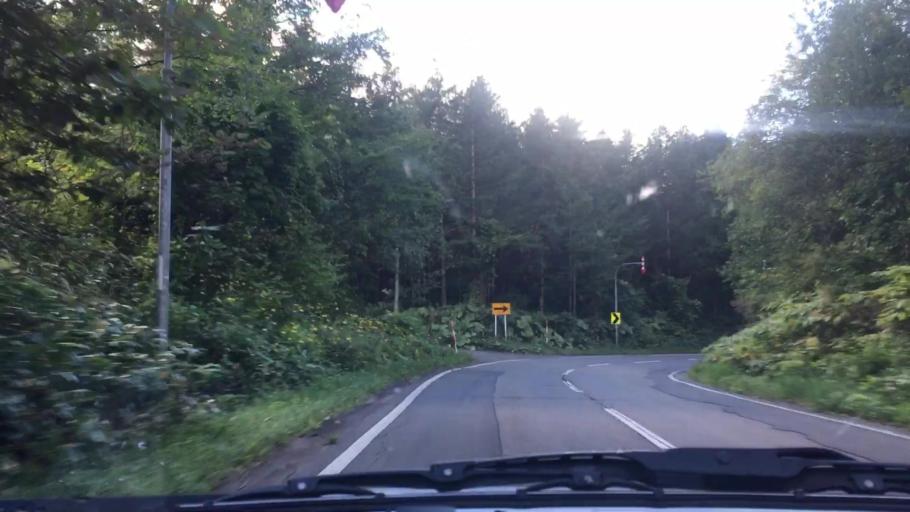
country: JP
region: Hokkaido
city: Otofuke
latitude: 43.1759
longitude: 142.9261
